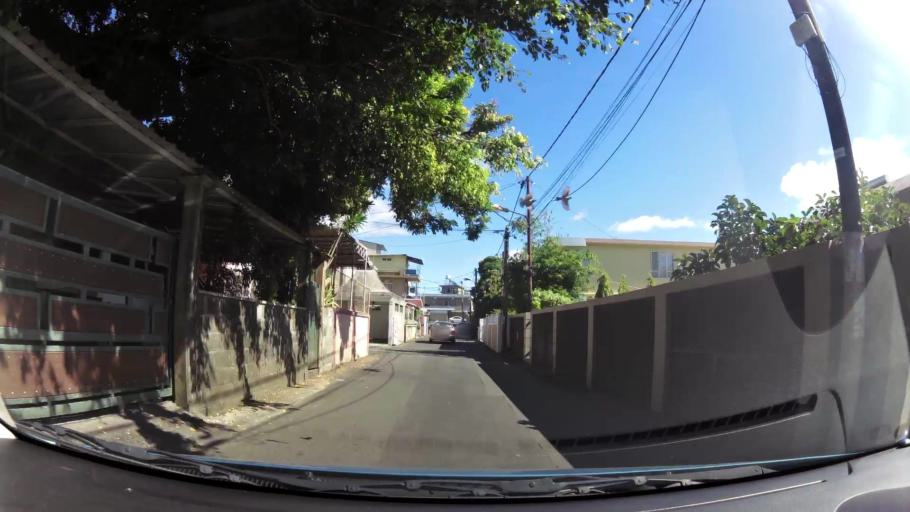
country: MU
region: Plaines Wilhems
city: Vacoas
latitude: -20.2961
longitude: 57.4844
